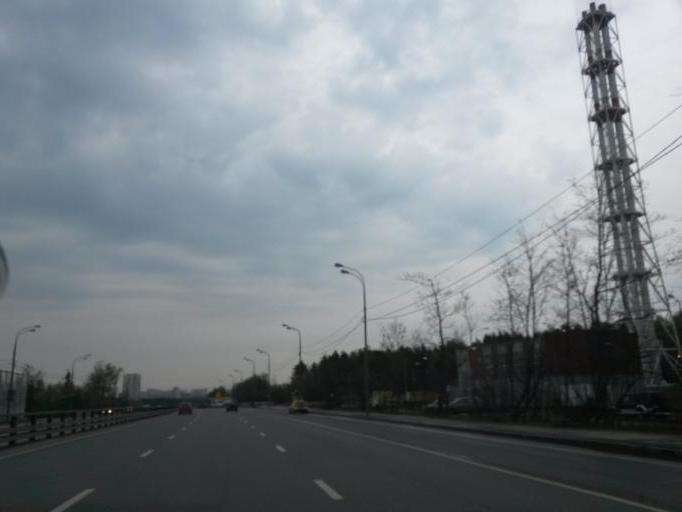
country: RU
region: Moscow
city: Annino
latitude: 55.5489
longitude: 37.5866
